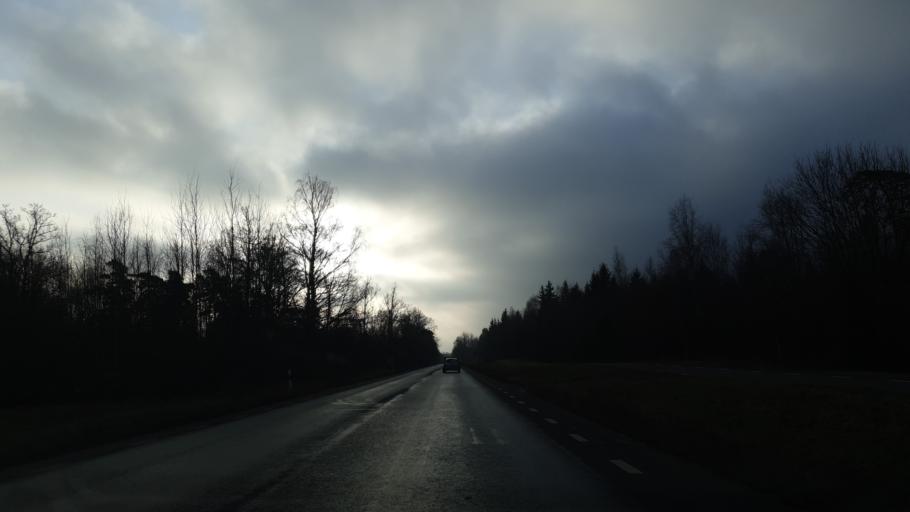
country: SE
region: Blekinge
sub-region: Karlshamns Kommun
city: Morrum
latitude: 56.1430
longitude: 14.6696
